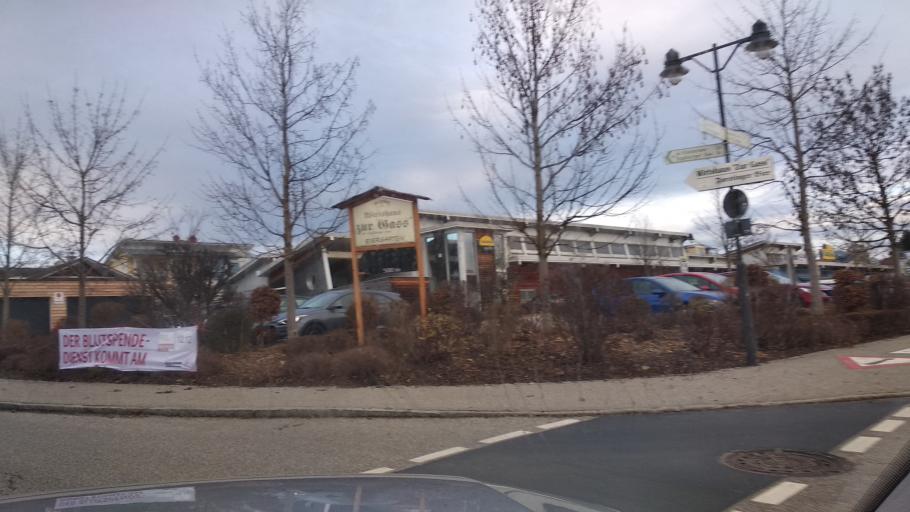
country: DE
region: Bavaria
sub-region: Upper Bavaria
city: Ebersberg
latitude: 48.0754
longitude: 11.9526
